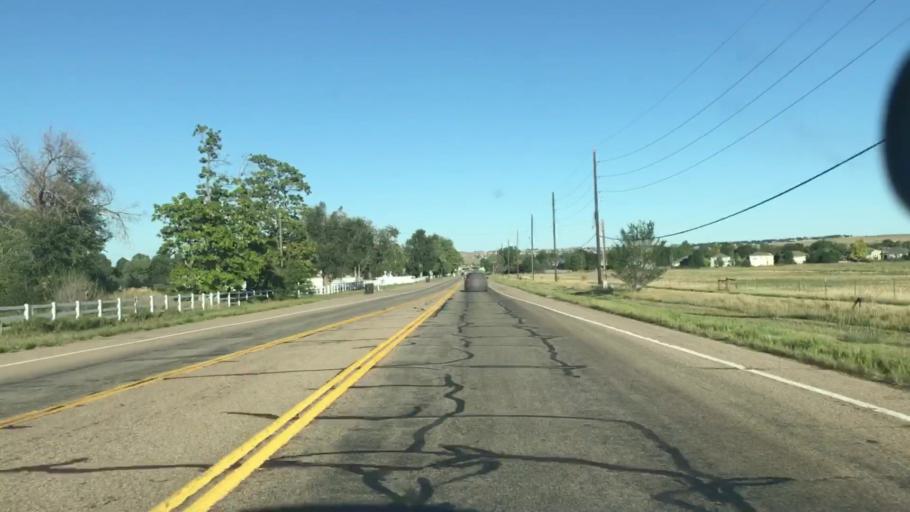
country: US
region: Colorado
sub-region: Boulder County
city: Lafayette
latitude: 39.9724
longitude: -105.1058
